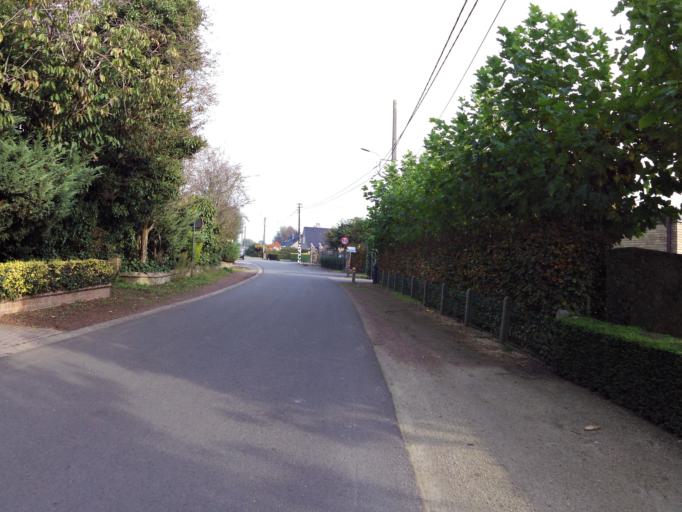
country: BE
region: Flanders
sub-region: Provincie West-Vlaanderen
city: Gistel
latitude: 51.1538
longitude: 2.9868
